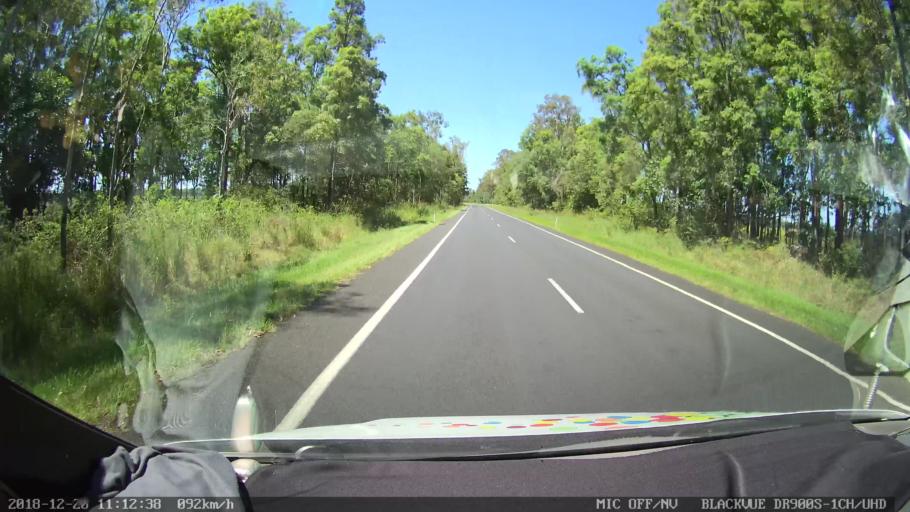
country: AU
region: New South Wales
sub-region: Richmond Valley
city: Casino
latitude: -28.9767
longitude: 153.0104
